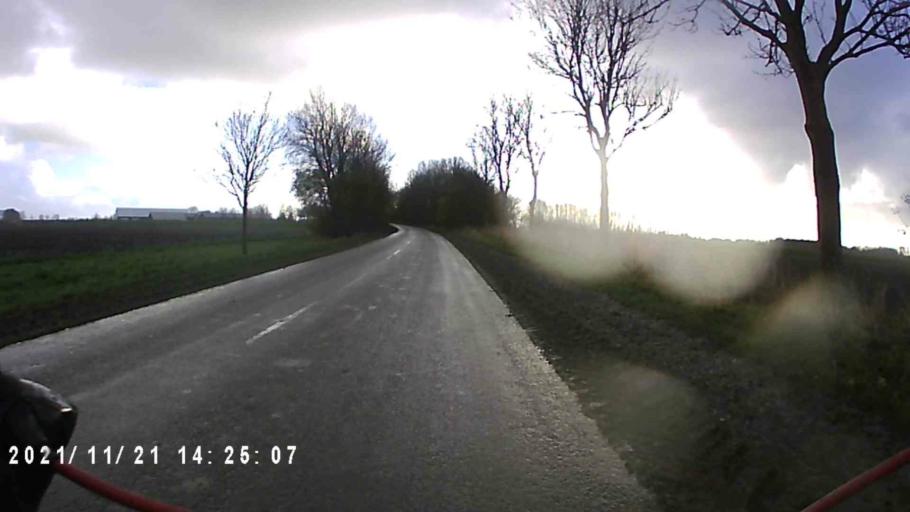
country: NL
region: Groningen
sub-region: Gemeente De Marne
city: Ulrum
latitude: 53.3682
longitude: 6.2926
